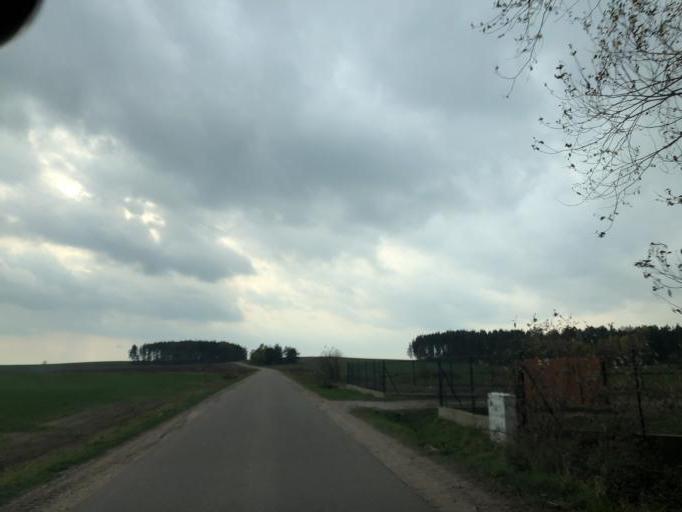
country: PL
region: Podlasie
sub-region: Lomza
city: Lomza
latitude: 53.1524
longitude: 21.9996
